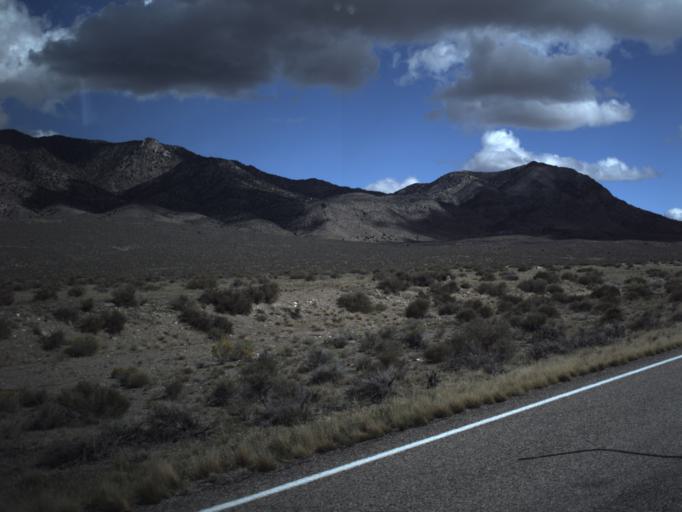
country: US
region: Utah
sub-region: Beaver County
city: Milford
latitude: 38.4455
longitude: -113.3305
